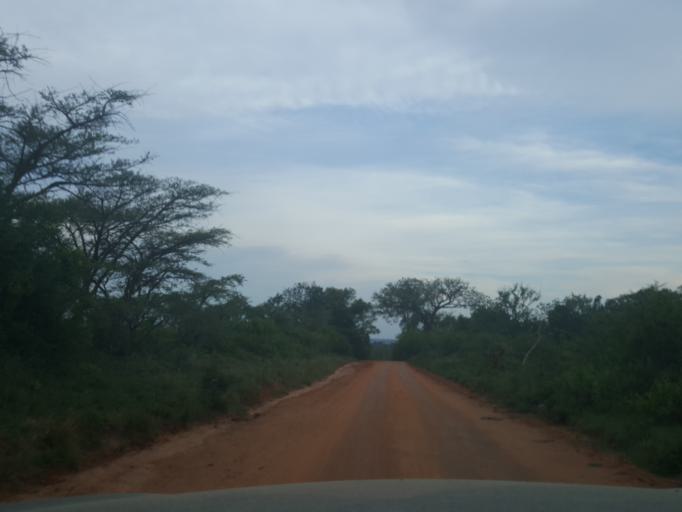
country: ZA
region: Limpopo
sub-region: Mopani District Municipality
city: Hoedspruit
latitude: -24.5880
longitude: 30.9577
